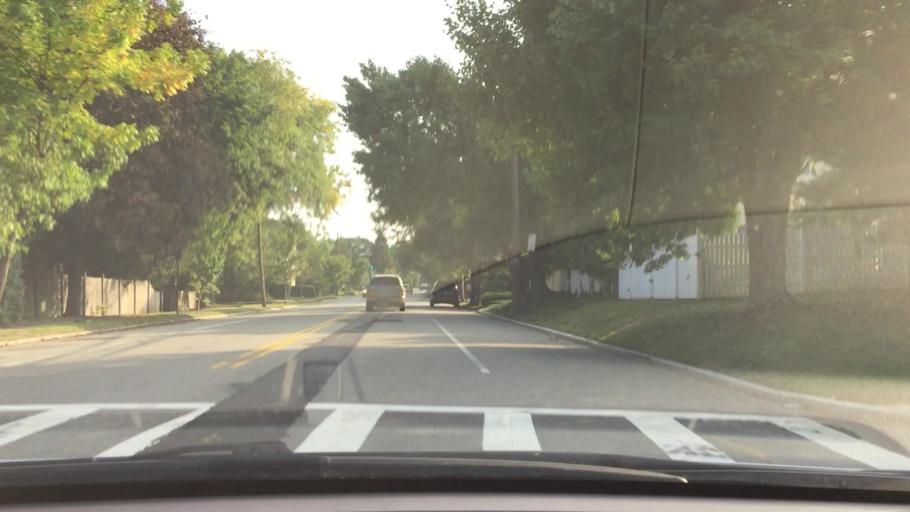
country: US
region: New Jersey
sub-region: Essex County
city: Montclair
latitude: 40.8306
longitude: -74.1976
